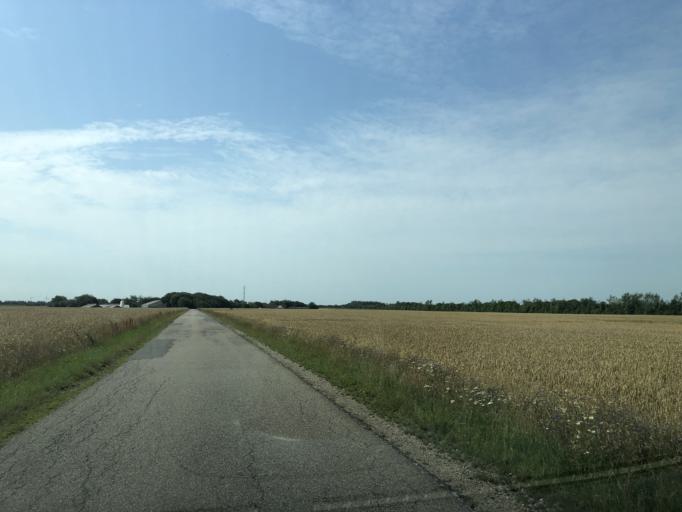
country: DK
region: Central Jutland
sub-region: Lemvig Kommune
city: Lemvig
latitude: 56.4434
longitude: 8.2892
